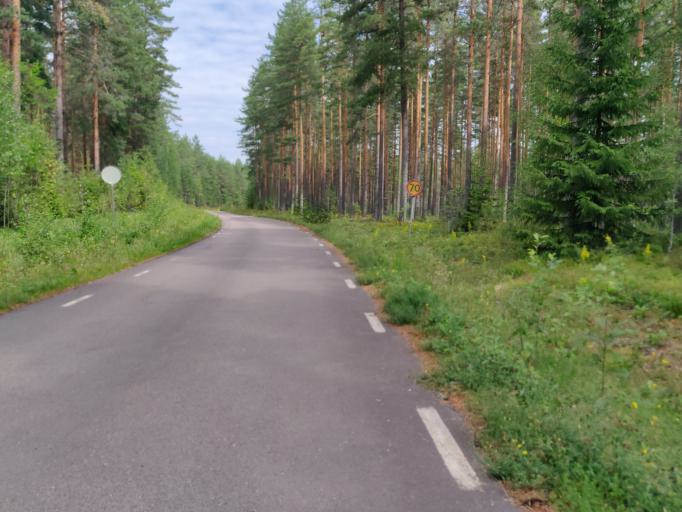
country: SE
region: Vaermland
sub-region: Munkfors Kommun
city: Munkfors
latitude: 59.9599
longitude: 13.5316
